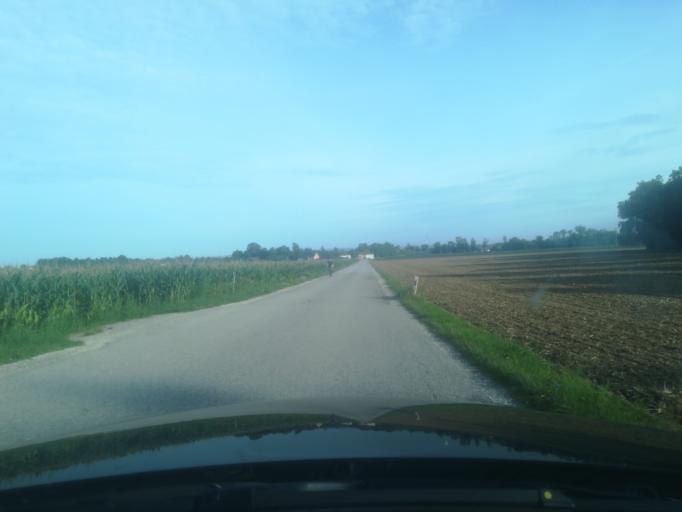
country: AT
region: Upper Austria
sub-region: Wels-Land
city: Marchtrenk
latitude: 48.1751
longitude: 14.1608
